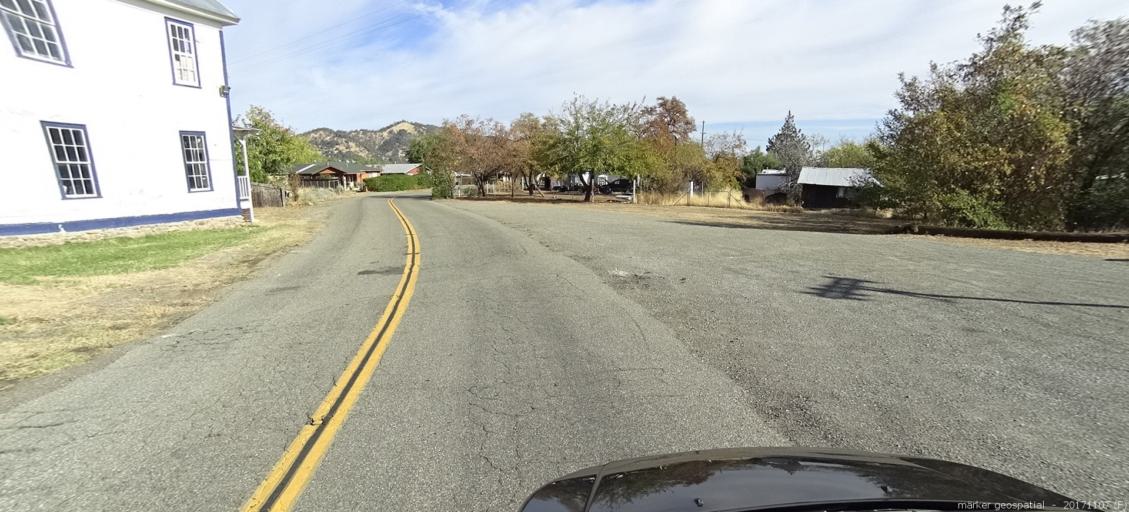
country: US
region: California
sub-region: Shasta County
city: Shasta
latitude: 40.5050
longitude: -122.5429
